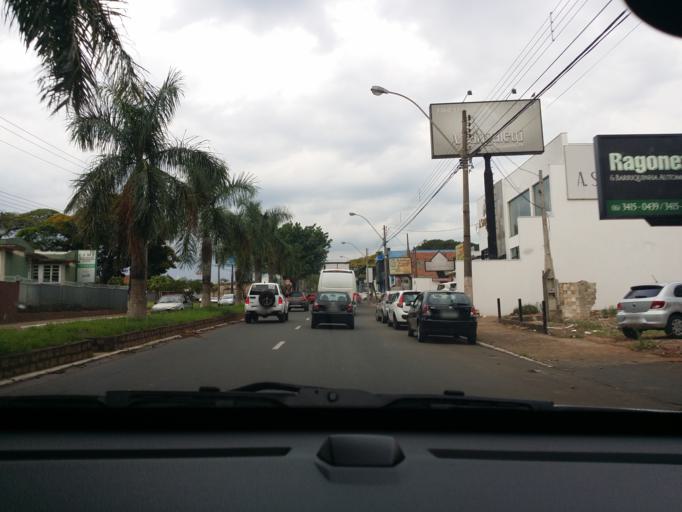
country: BR
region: Sao Paulo
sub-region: Sao Carlos
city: Sao Carlos
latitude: -22.0327
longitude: -47.8871
